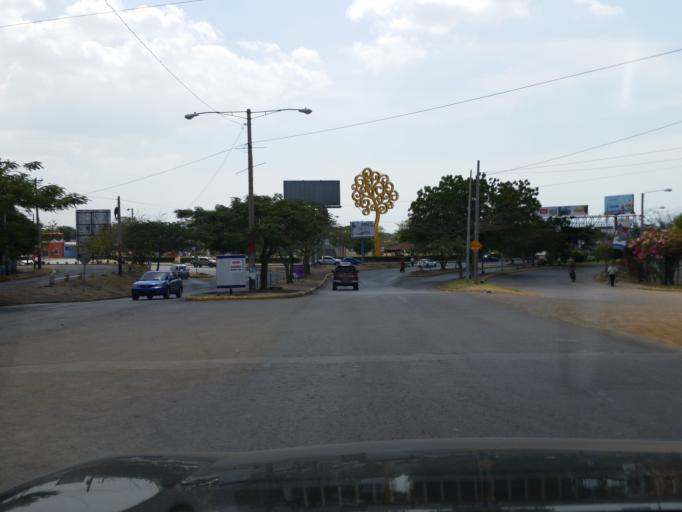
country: NI
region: Managua
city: Managua
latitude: 12.1424
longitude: -86.2231
